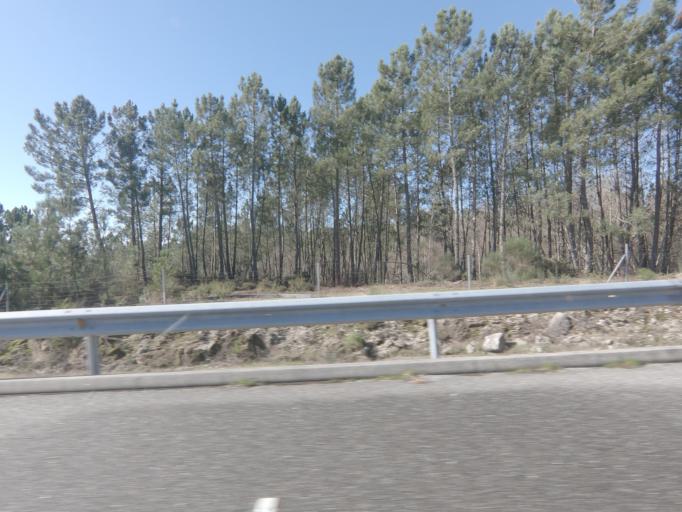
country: ES
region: Galicia
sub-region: Provincia de Ourense
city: Pinor
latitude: 42.4853
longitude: -8.0218
